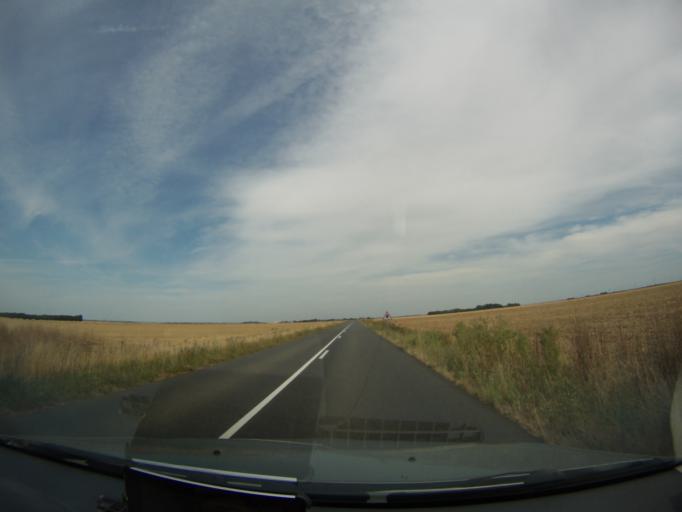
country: FR
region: Poitou-Charentes
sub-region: Departement des Deux-Sevres
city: Airvault
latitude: 46.8116
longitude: -0.0632
